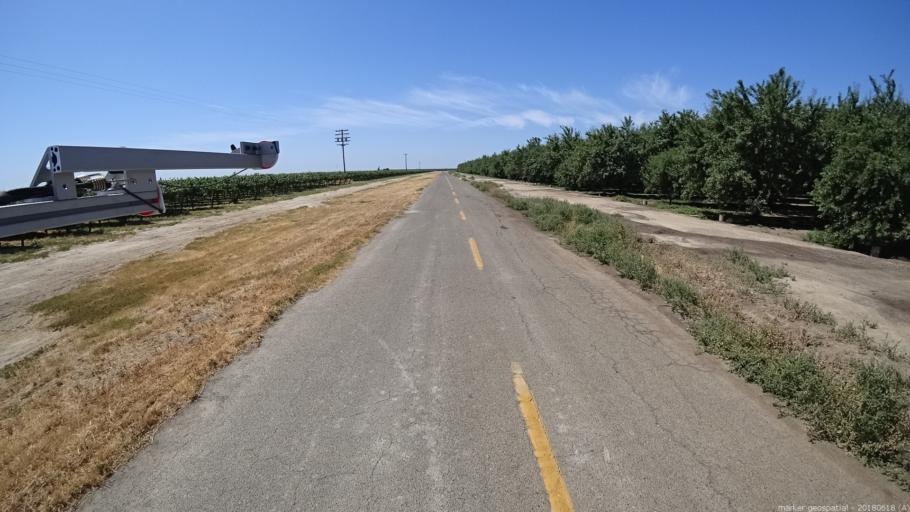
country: US
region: California
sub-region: Madera County
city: Parkwood
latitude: 36.8467
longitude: -120.1828
